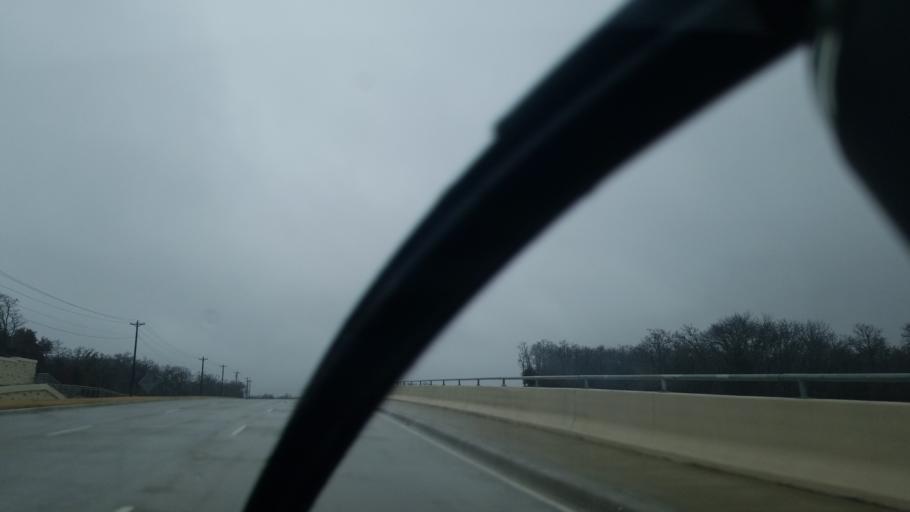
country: US
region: Texas
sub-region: Denton County
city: Corinth
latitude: 33.1387
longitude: -97.0959
